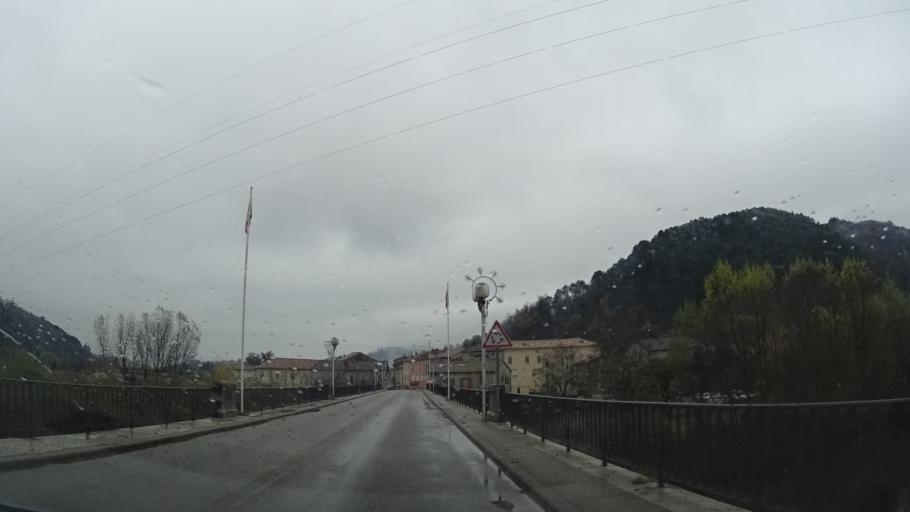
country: FR
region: Rhone-Alpes
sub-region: Departement de l'Ardeche
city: Labegude
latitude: 44.6517
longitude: 4.3654
